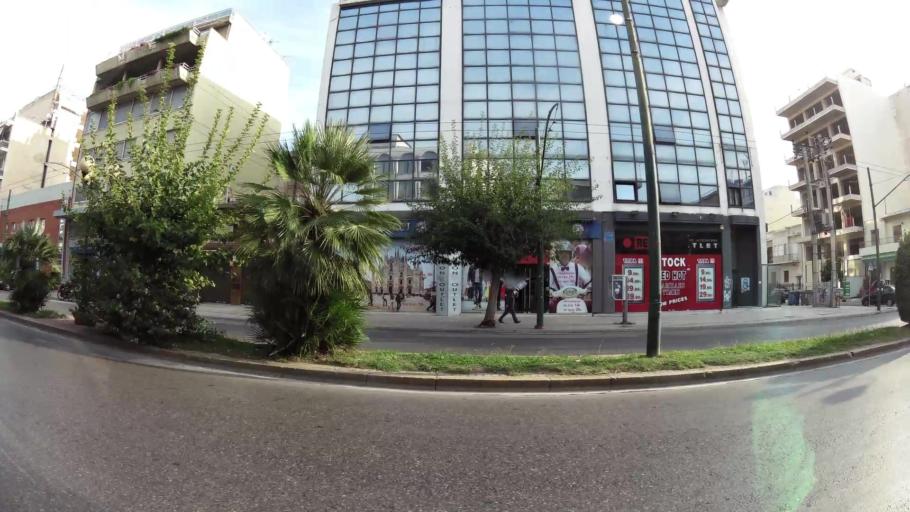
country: GR
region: Attica
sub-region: Nomarchia Athinas
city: Peristeri
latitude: 38.0002
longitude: 23.7073
